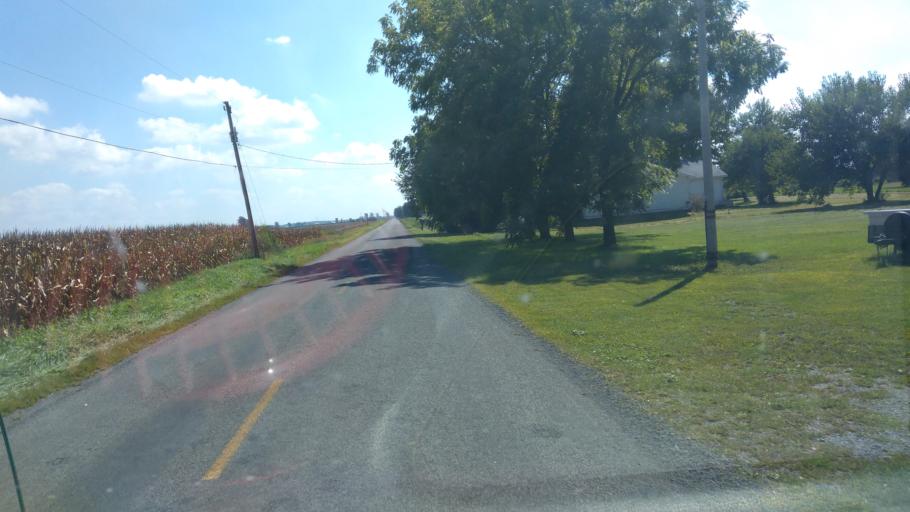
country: US
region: Ohio
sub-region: Hardin County
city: Ada
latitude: 40.7013
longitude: -83.8421
